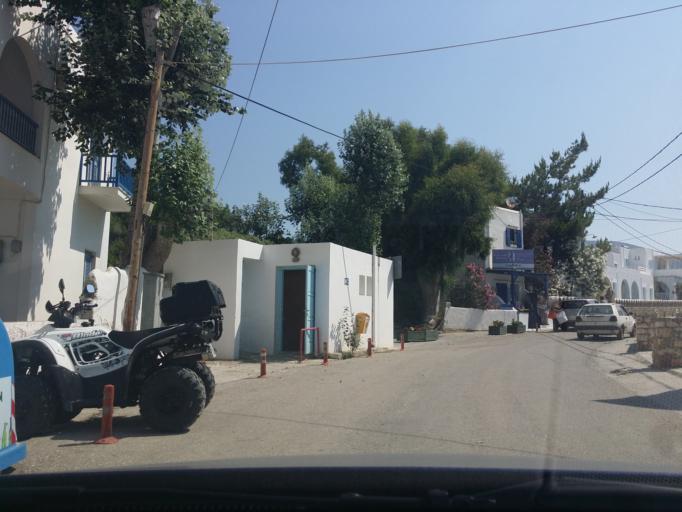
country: GR
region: South Aegean
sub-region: Nomos Kykladon
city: Antiparos
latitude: 36.9967
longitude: 25.1369
